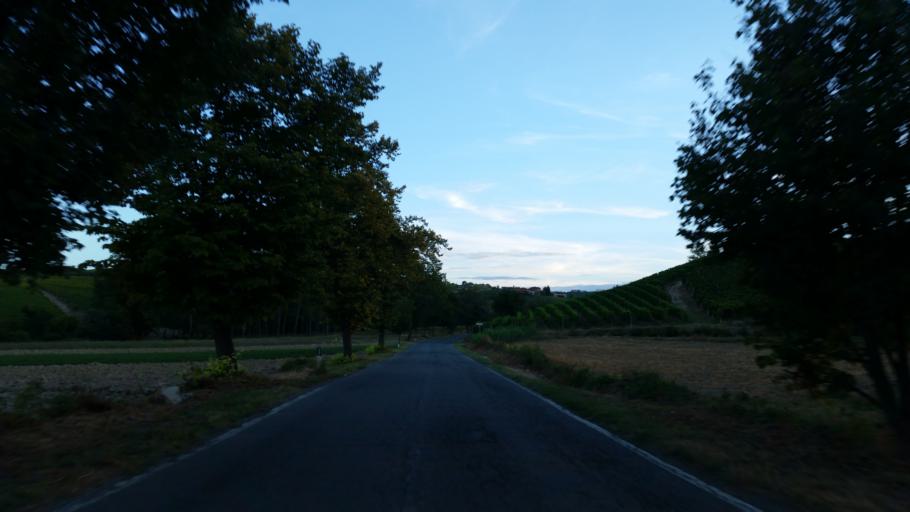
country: IT
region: Piedmont
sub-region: Provincia di Asti
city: Calosso
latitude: 44.7487
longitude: 8.2064
